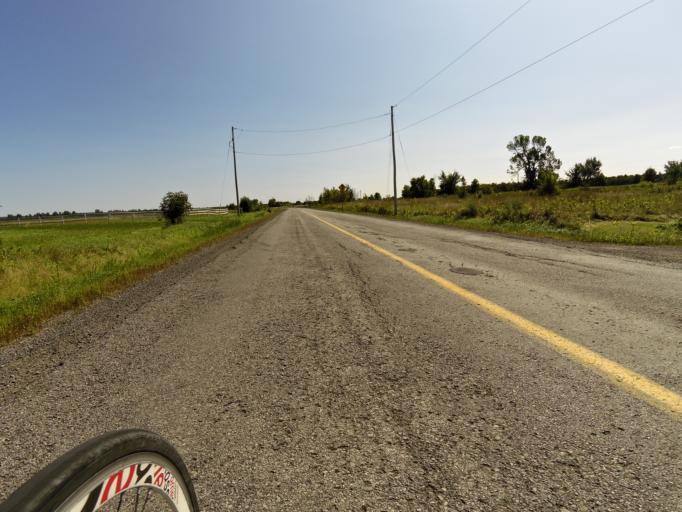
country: CA
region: Ontario
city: Arnprior
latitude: 45.4507
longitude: -76.0844
